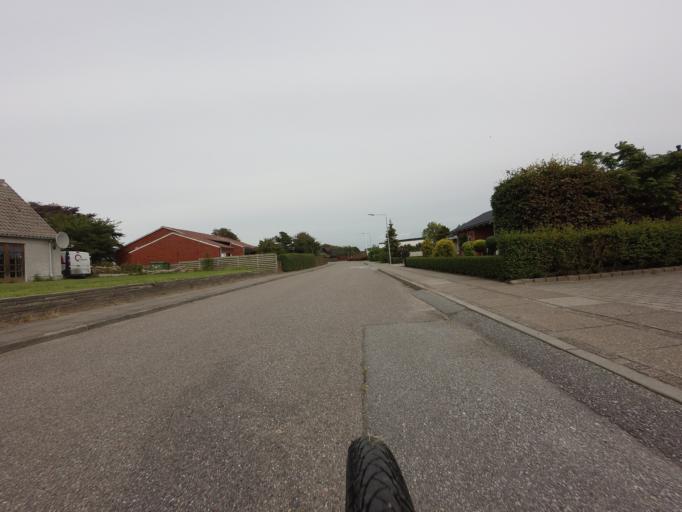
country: DK
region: North Denmark
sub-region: Hjorring Kommune
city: Vra
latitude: 57.4261
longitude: 9.8405
